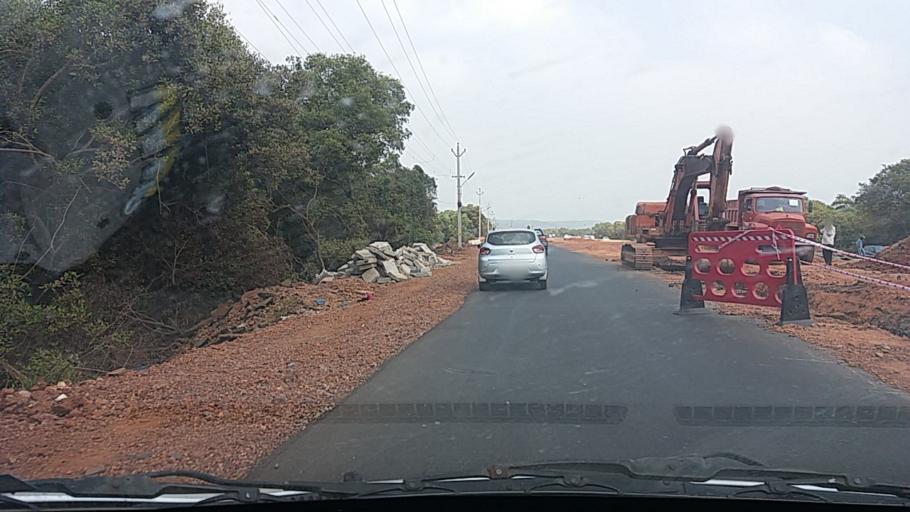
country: IN
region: Goa
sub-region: North Goa
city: Bambolim
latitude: 15.4806
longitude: 73.8478
